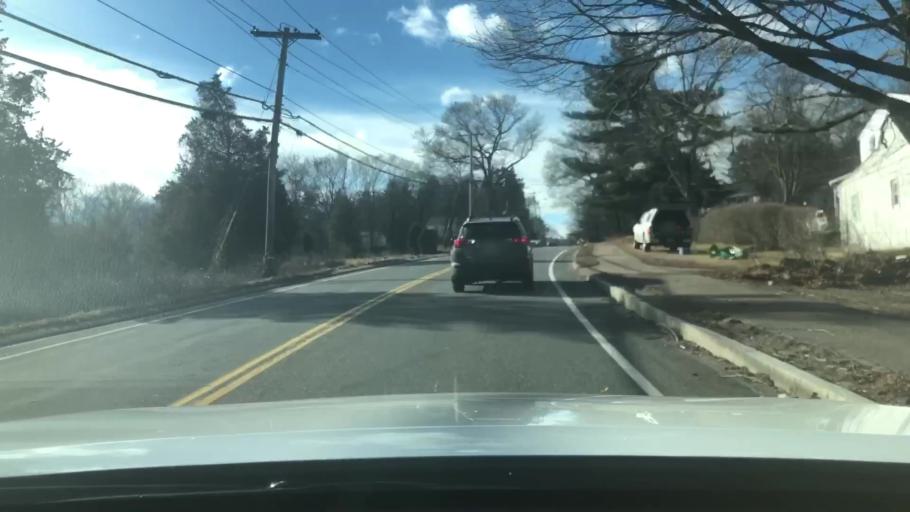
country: US
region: Massachusetts
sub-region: Norfolk County
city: Bellingham
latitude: 42.0658
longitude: -71.4768
